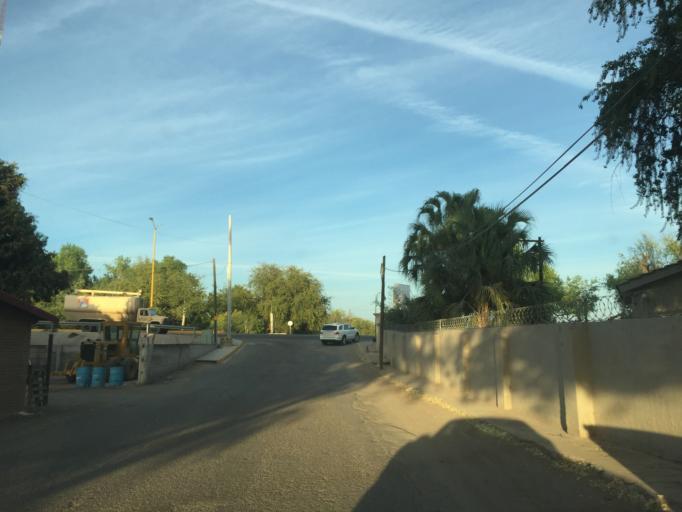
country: MX
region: Sonora
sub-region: Navojoa
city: Guaymitas
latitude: 27.0996
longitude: -109.4480
